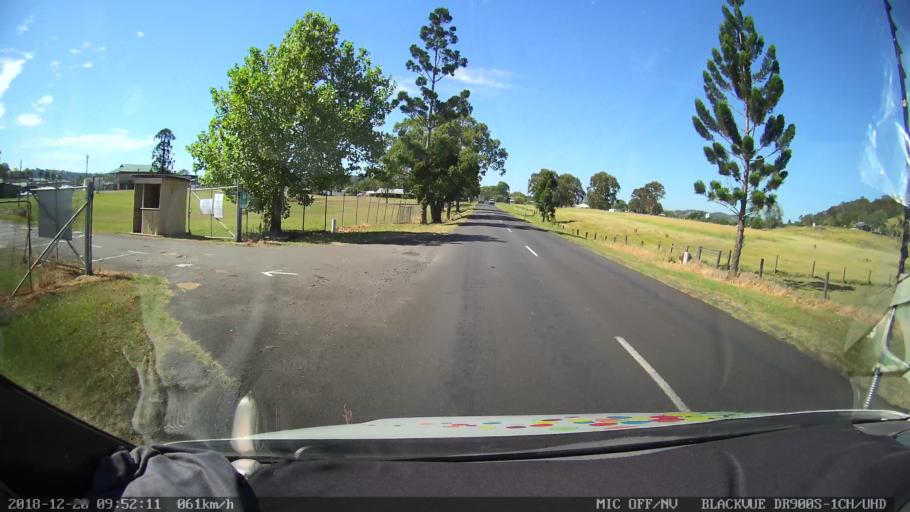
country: AU
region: New South Wales
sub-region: Lismore Municipality
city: Lismore
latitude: -28.7938
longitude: 153.2720
